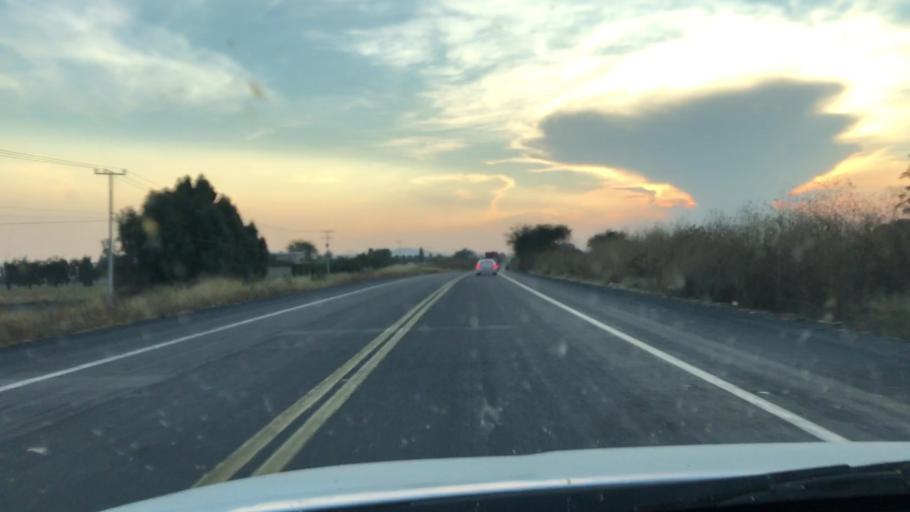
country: MX
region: Michoacan
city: Tanhuato de Guerrero
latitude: 20.3076
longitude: -102.3150
